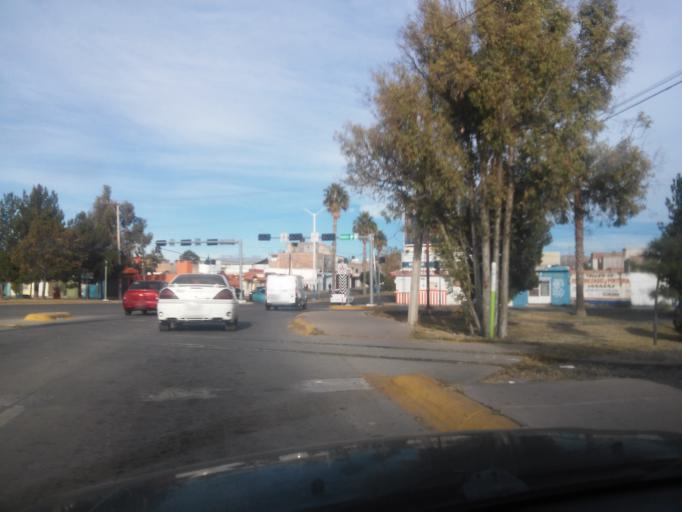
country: MX
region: Durango
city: Victoria de Durango
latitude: 24.0382
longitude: -104.6548
